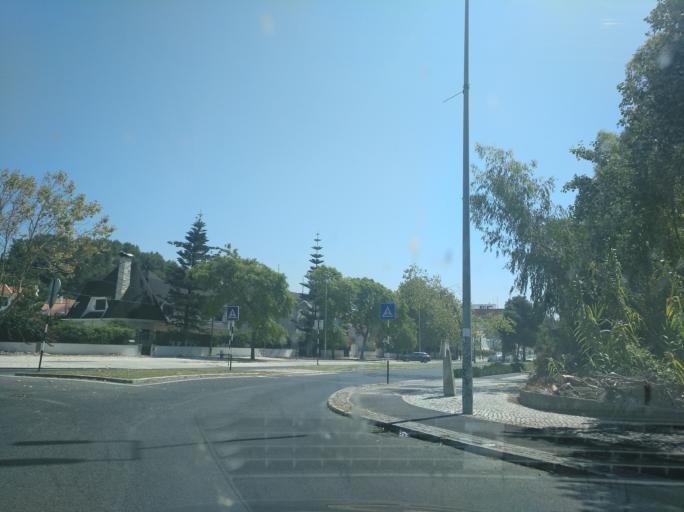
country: PT
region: Setubal
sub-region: Almada
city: Trafaria
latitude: 38.6640
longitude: -9.2438
